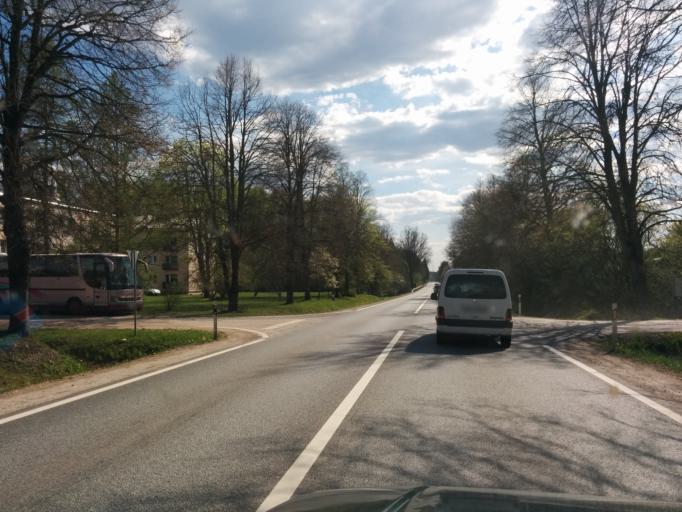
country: LV
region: Seja
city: Loja
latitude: 57.1437
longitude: 24.6753
